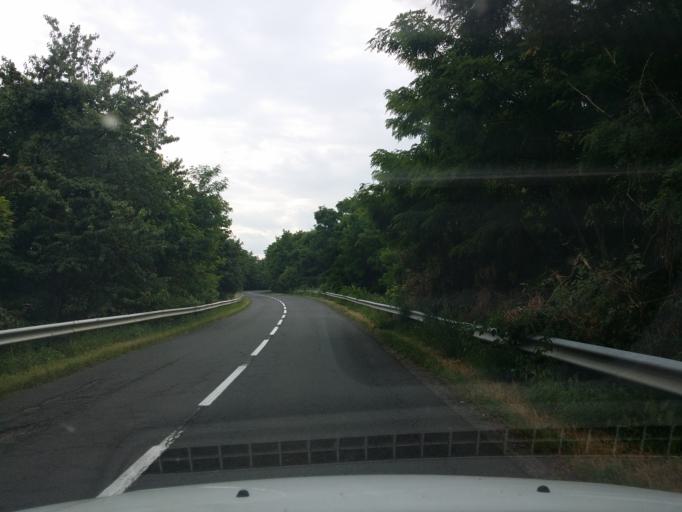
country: HU
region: Nograd
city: Bercel
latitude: 47.9314
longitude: 19.3649
